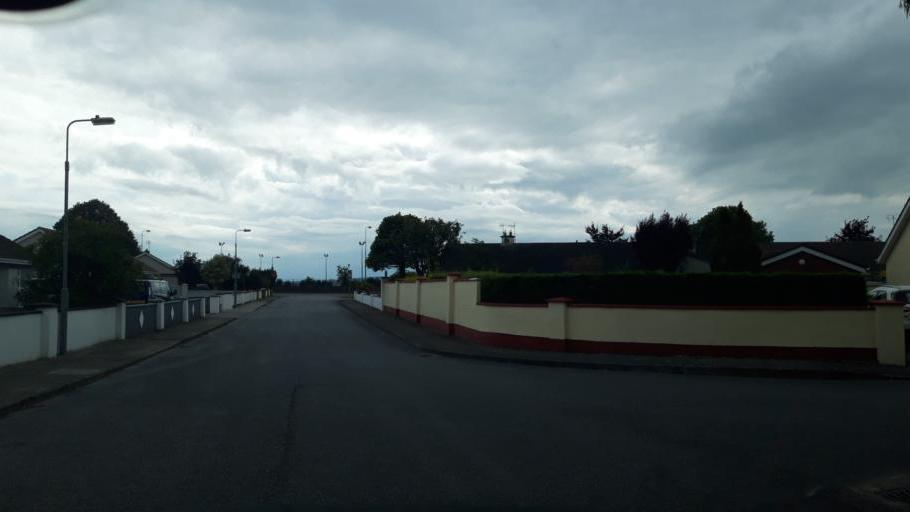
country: IE
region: Leinster
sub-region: Kilkenny
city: Ballyragget
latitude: 52.7824
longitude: -7.3309
